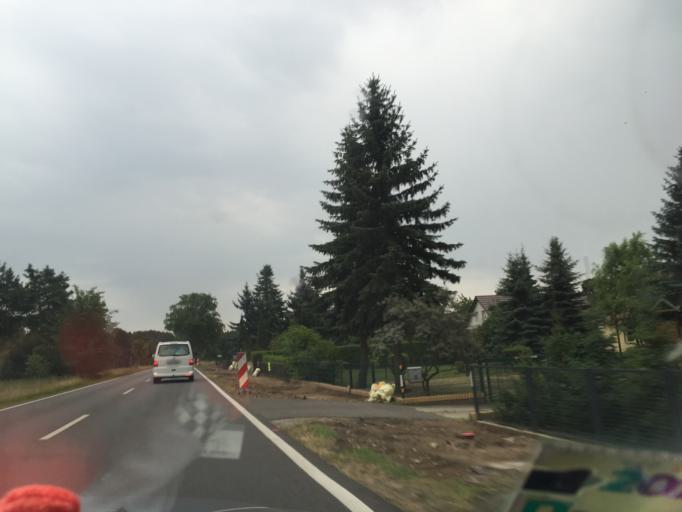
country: DE
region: Brandenburg
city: Zehdenick
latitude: 52.9629
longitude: 13.3678
